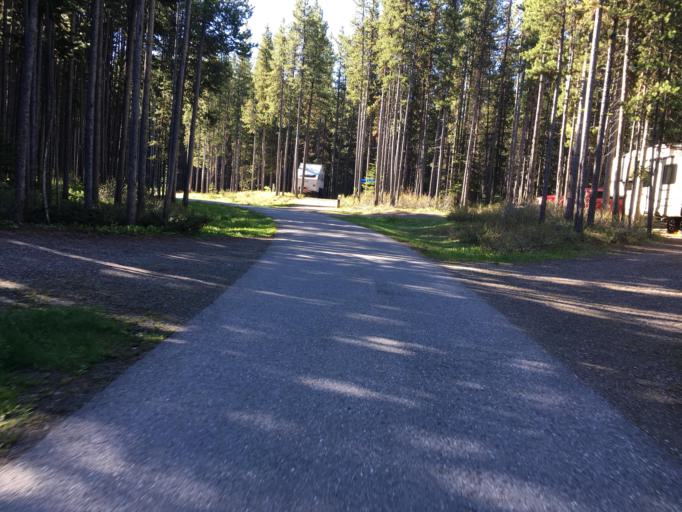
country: CA
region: Alberta
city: Canmore
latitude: 50.6352
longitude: -115.0995
